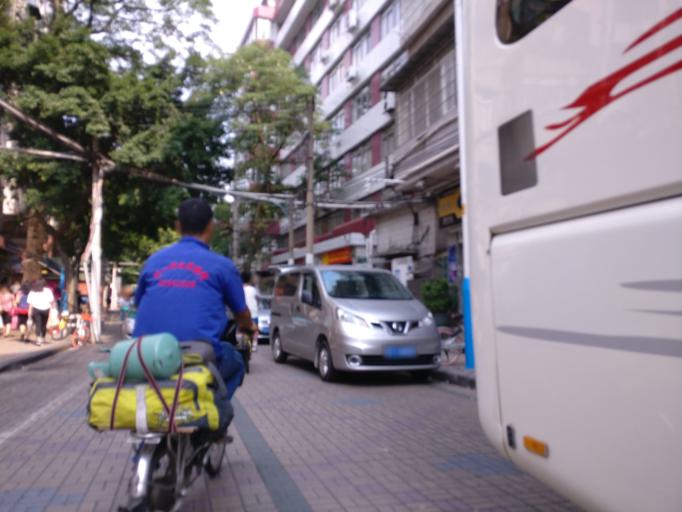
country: CN
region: Guangdong
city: Guangzhou
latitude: 23.1240
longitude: 113.2905
